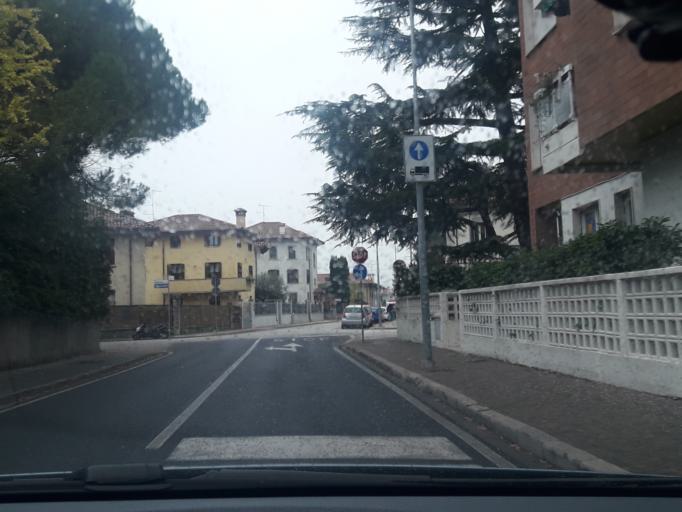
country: IT
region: Friuli Venezia Giulia
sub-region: Provincia di Udine
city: Udine
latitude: 46.0575
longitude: 13.2249
